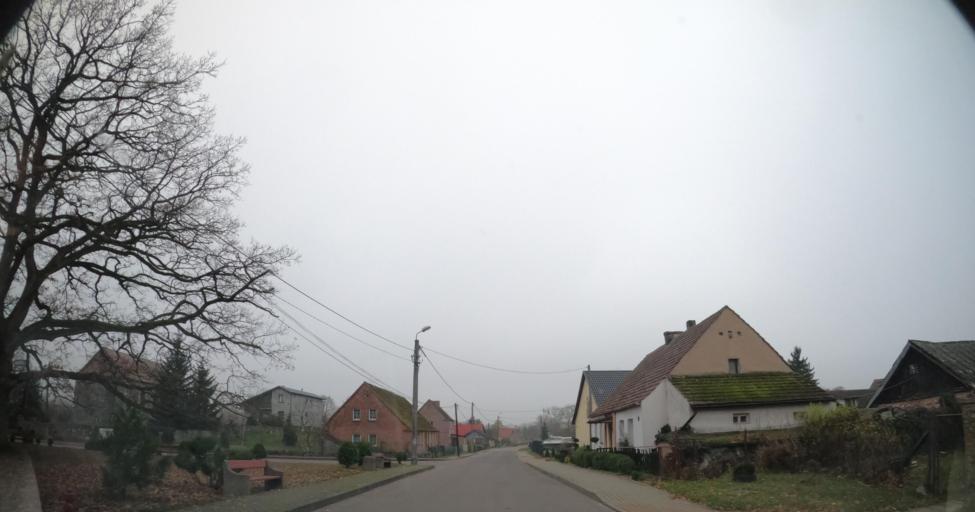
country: PL
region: West Pomeranian Voivodeship
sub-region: Powiat drawski
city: Drawsko Pomorskie
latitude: 53.5714
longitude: 15.8398
